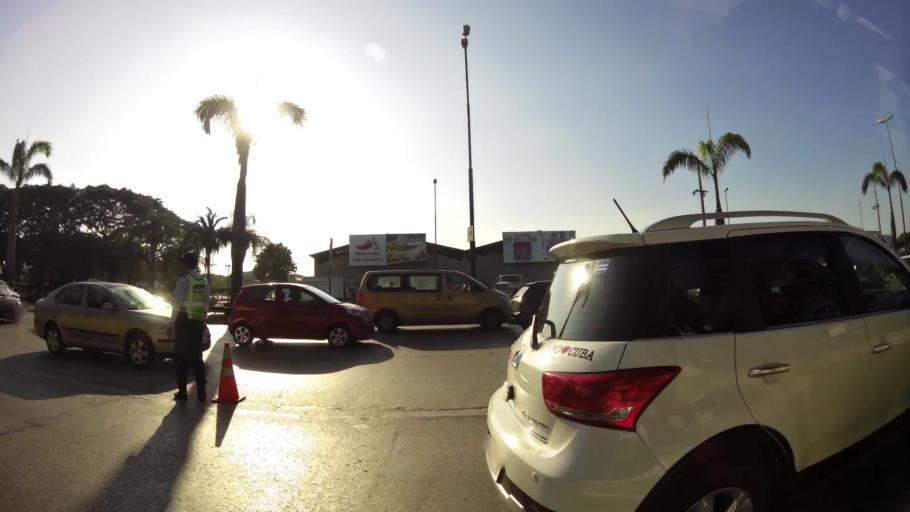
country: EC
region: Guayas
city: Eloy Alfaro
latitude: -2.1684
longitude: -79.8799
